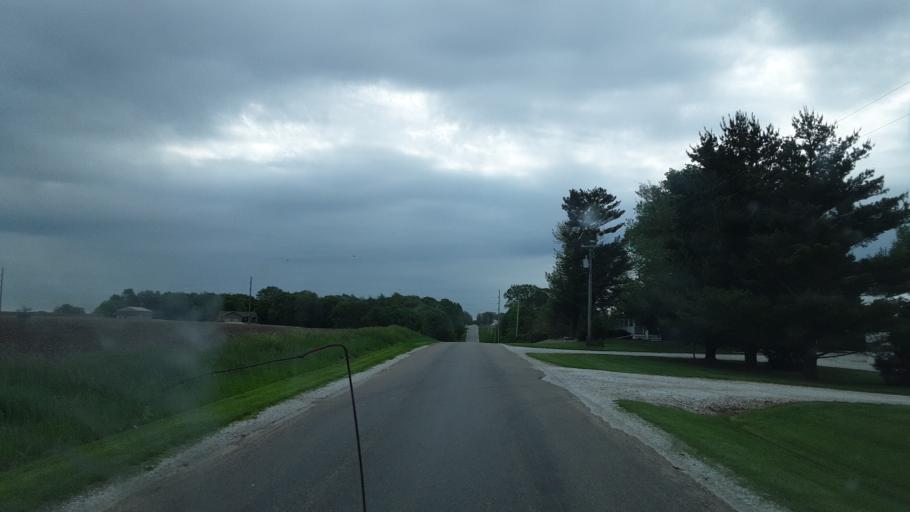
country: US
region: Illinois
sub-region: Fulton County
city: Astoria
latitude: 40.3640
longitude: -90.4406
